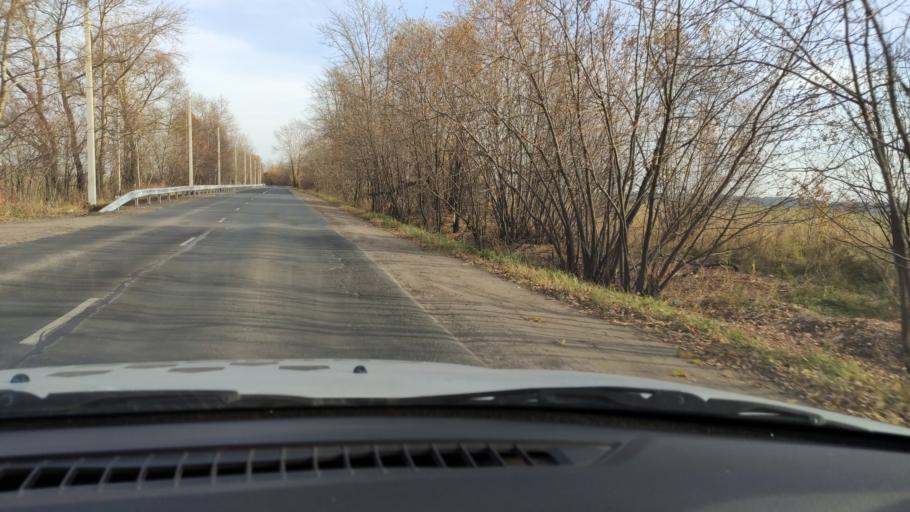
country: RU
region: Perm
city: Perm
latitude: 58.0351
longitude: 56.3651
